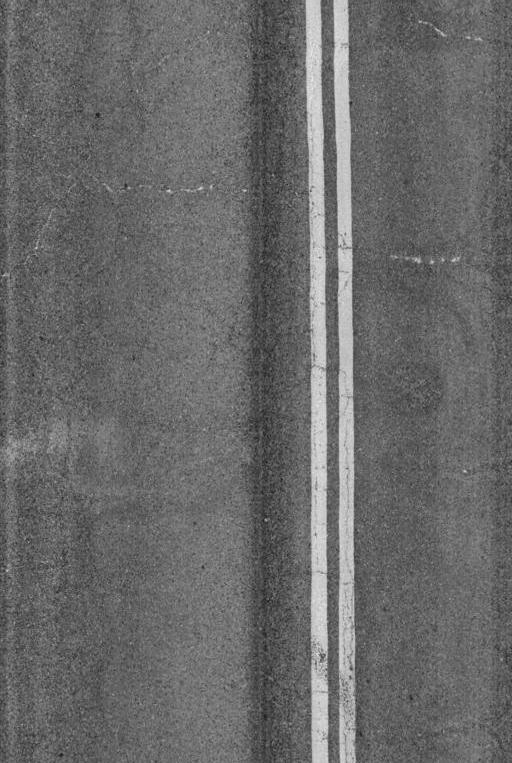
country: US
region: Maryland
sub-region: Montgomery County
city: Chevy Chase
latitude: 38.9516
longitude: -77.0508
